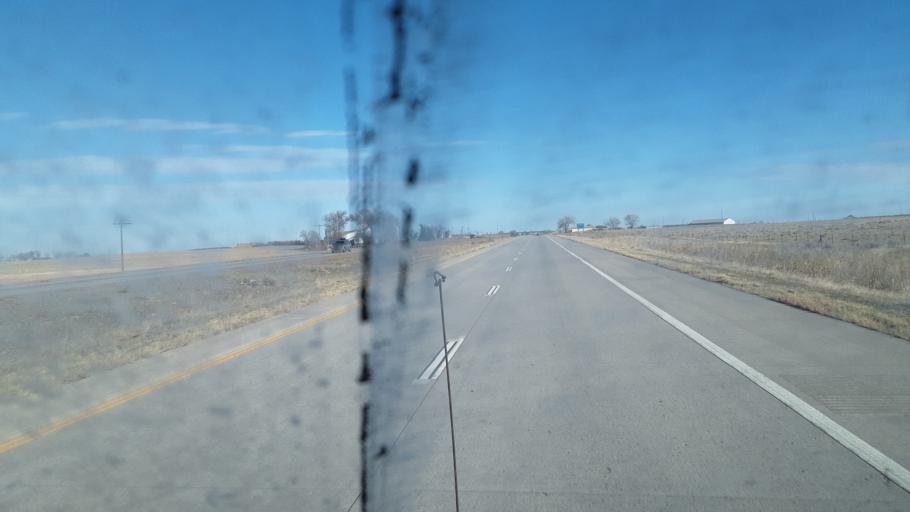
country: US
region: Colorado
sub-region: Morgan County
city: Fort Morgan
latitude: 40.2321
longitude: -104.1101
